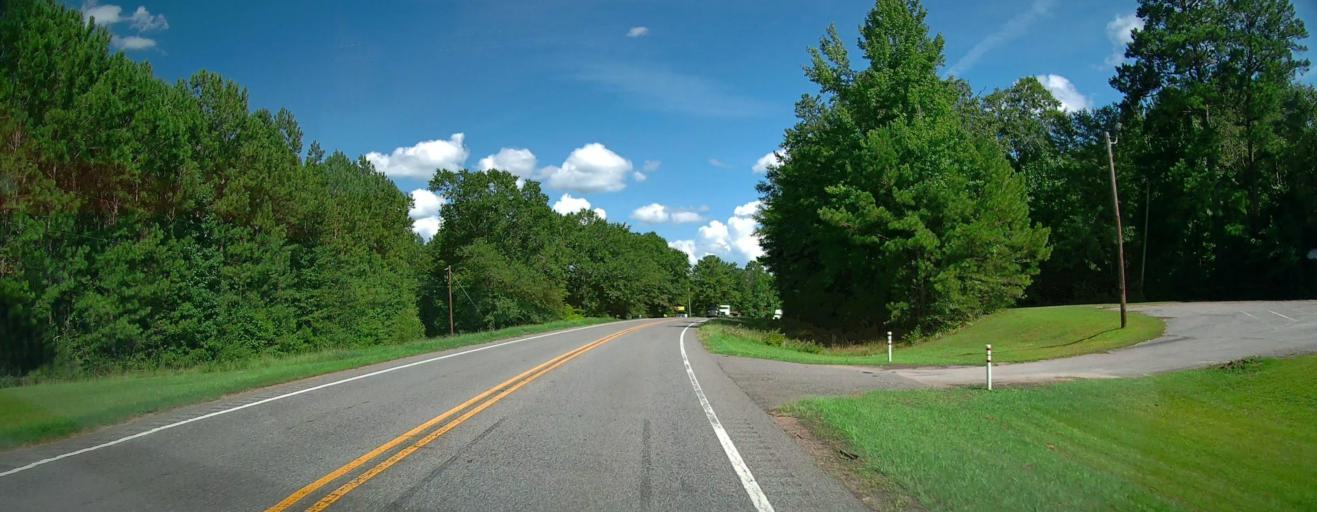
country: US
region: Alabama
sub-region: Pickens County
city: Gordo
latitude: 33.3315
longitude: -87.9149
